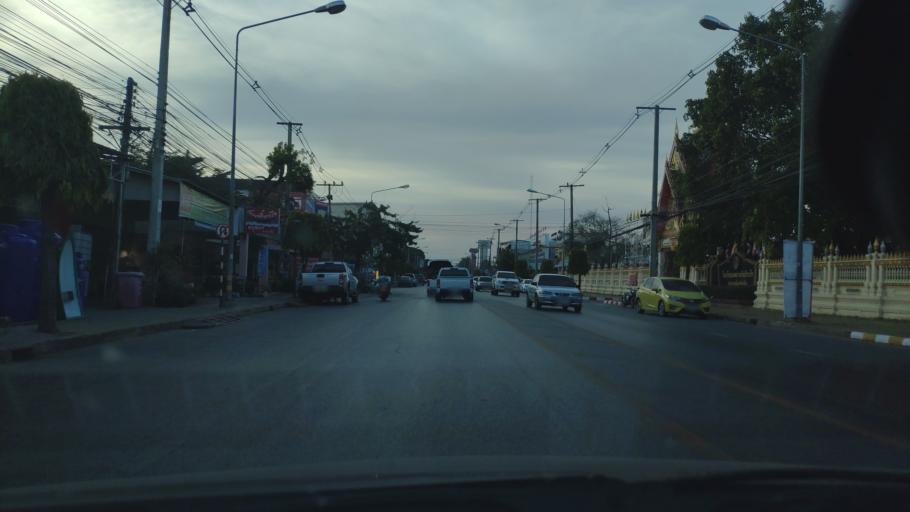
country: TH
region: Roi Et
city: Roi Et
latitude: 16.0559
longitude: 103.6381
